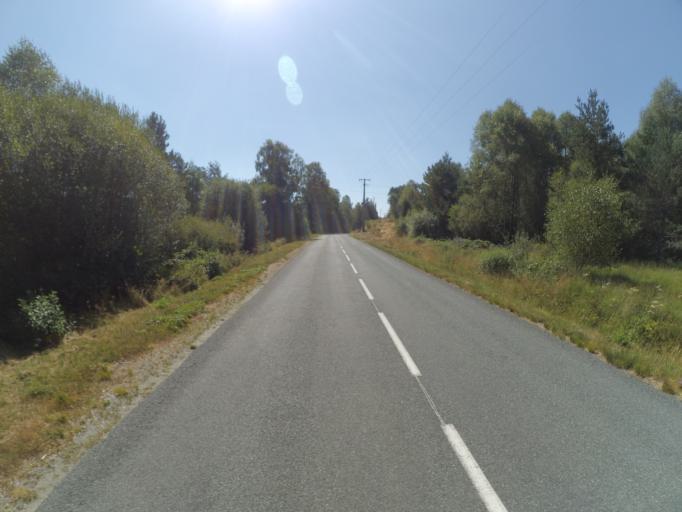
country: FR
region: Limousin
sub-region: Departement de la Haute-Vienne
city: Peyrat-le-Chateau
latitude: 45.8649
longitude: 1.9000
